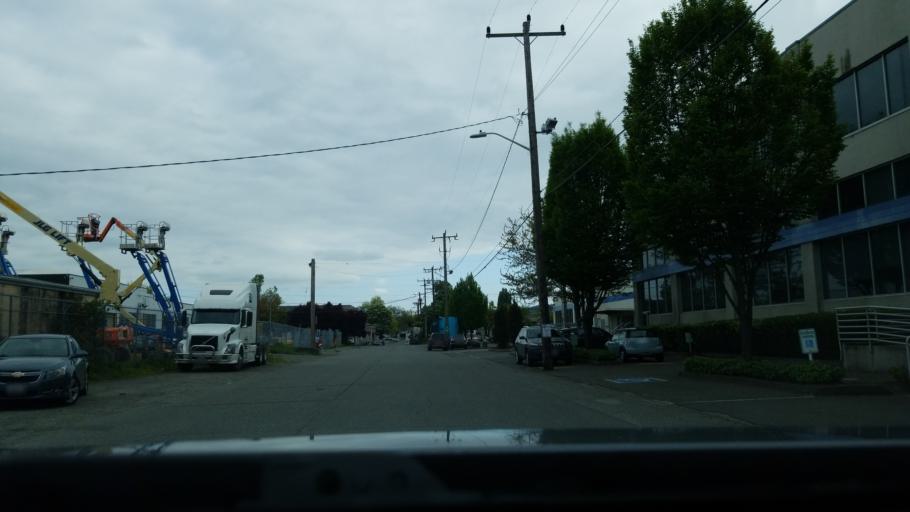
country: US
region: Washington
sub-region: King County
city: White Center
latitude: 47.5569
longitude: -122.3310
